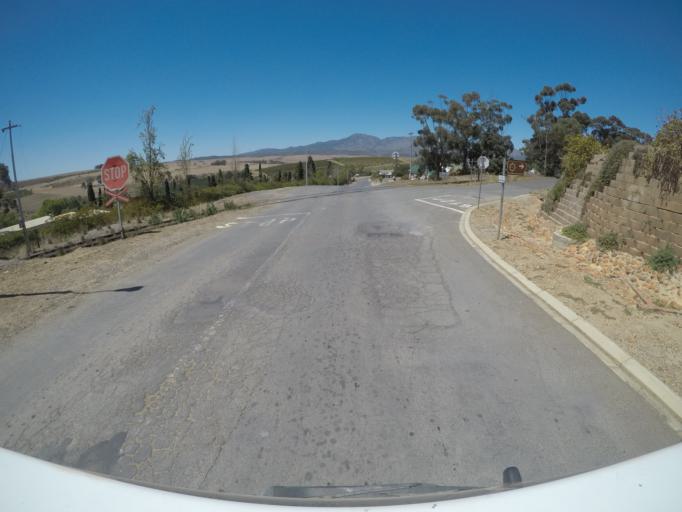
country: ZA
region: Western Cape
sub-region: Overberg District Municipality
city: Hermanus
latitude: -34.2246
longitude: 19.2061
